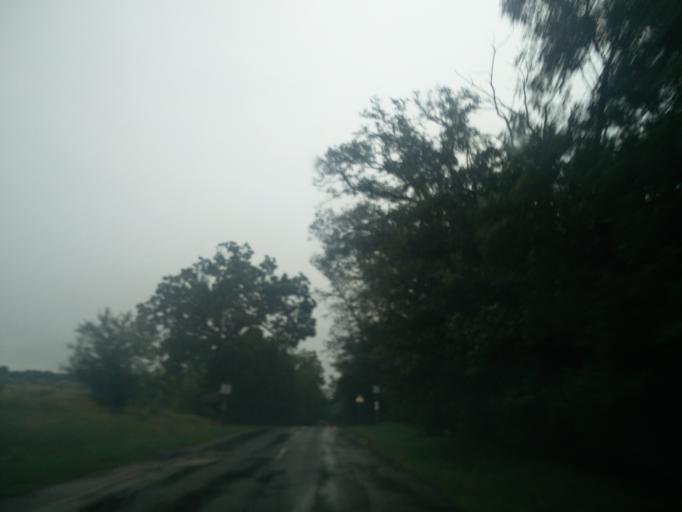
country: HU
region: Fejer
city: Bicske
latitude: 47.4328
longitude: 18.6220
